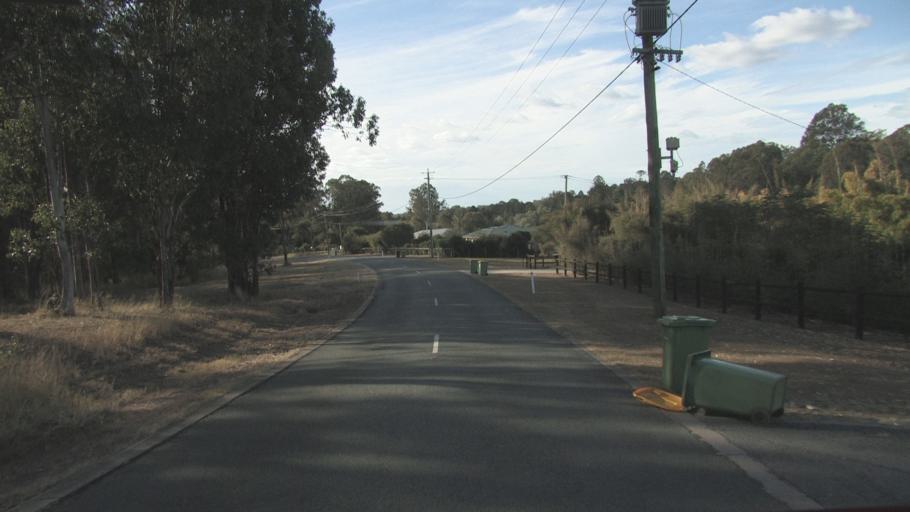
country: AU
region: Queensland
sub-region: Logan
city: Cedar Vale
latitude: -27.8821
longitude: 153.0104
